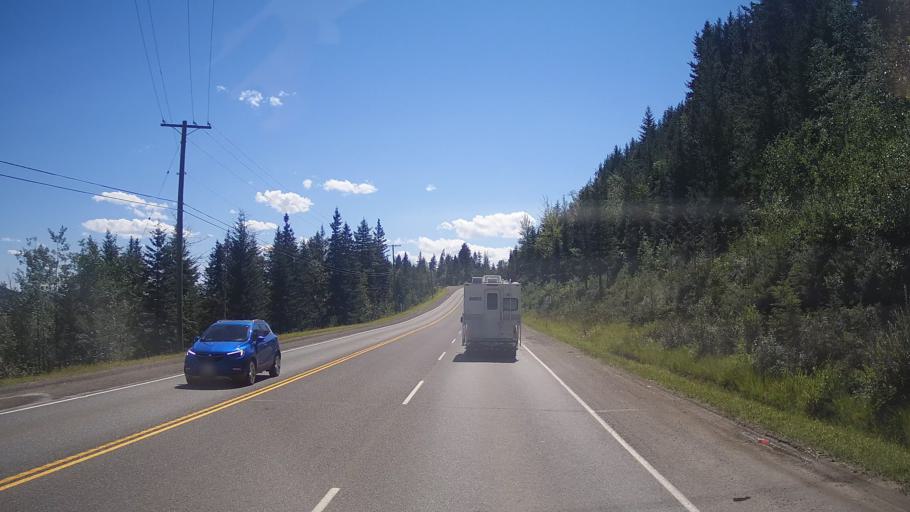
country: CA
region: British Columbia
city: Cache Creek
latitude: 51.6248
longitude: -121.2983
